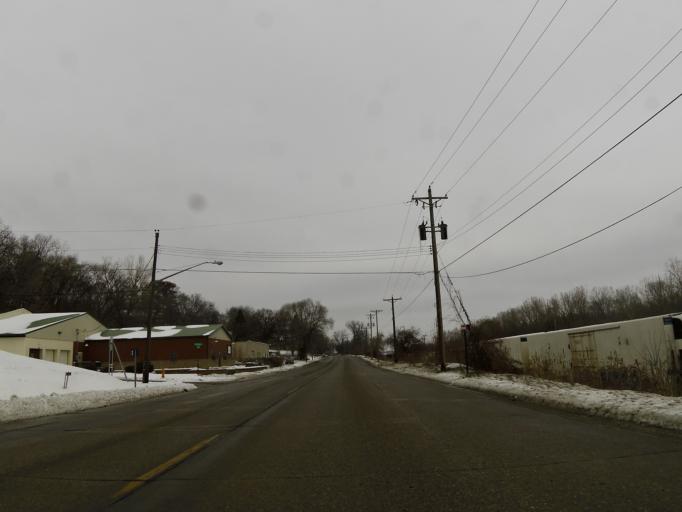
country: US
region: Minnesota
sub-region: Dakota County
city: South Saint Paul
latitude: 44.9158
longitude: -93.0562
